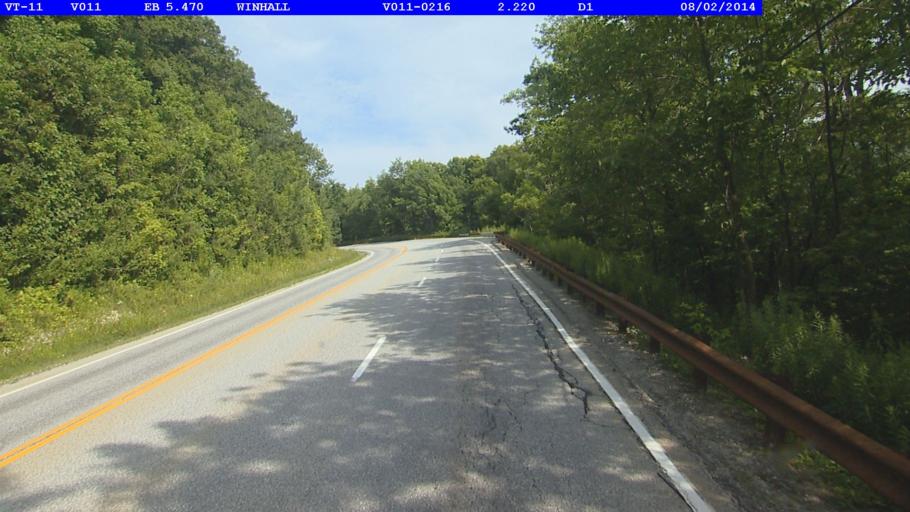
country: US
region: Vermont
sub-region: Bennington County
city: Manchester Center
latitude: 43.2055
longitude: -72.9777
